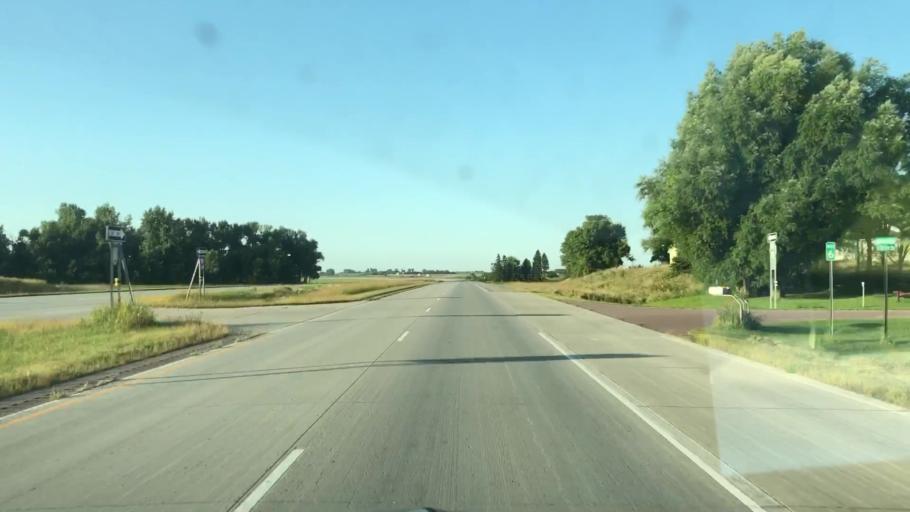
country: US
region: Minnesota
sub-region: Nobles County
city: Worthington
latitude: 43.5810
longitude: -95.6502
